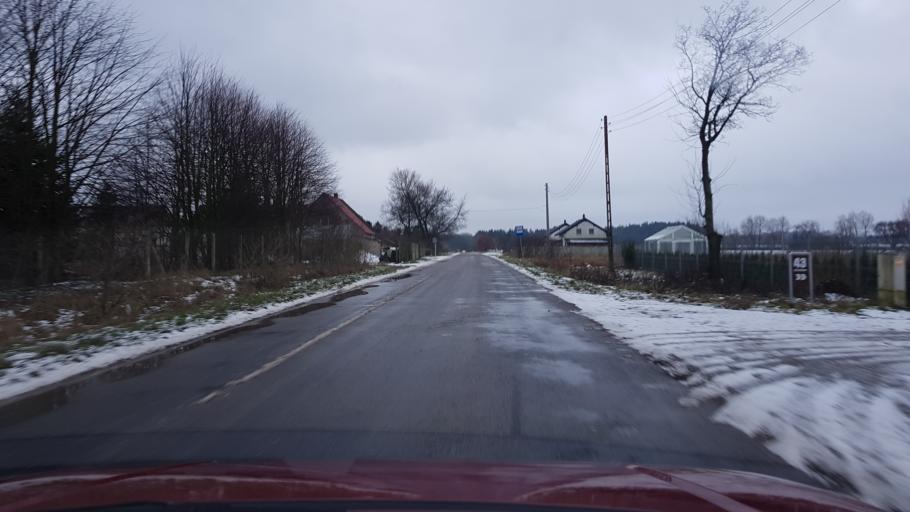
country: PL
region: West Pomeranian Voivodeship
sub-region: Powiat goleniowski
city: Nowogard
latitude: 53.6468
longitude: 15.1227
